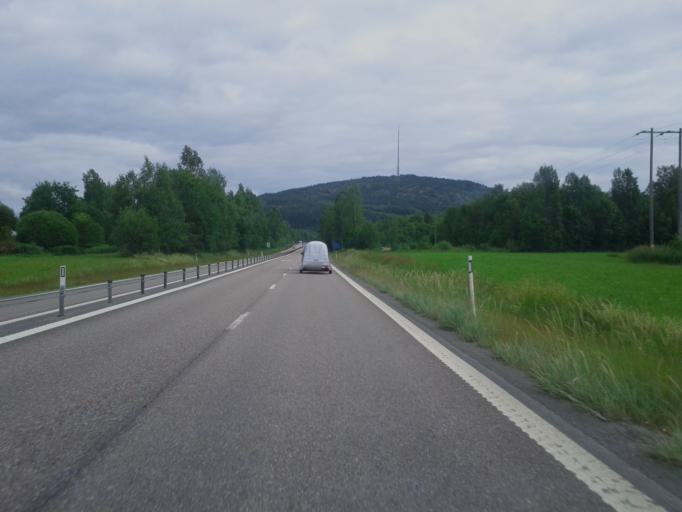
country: SE
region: Vaesternorrland
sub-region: OErnskoeldsviks Kommun
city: Ornskoldsvik
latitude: 63.2912
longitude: 18.6233
